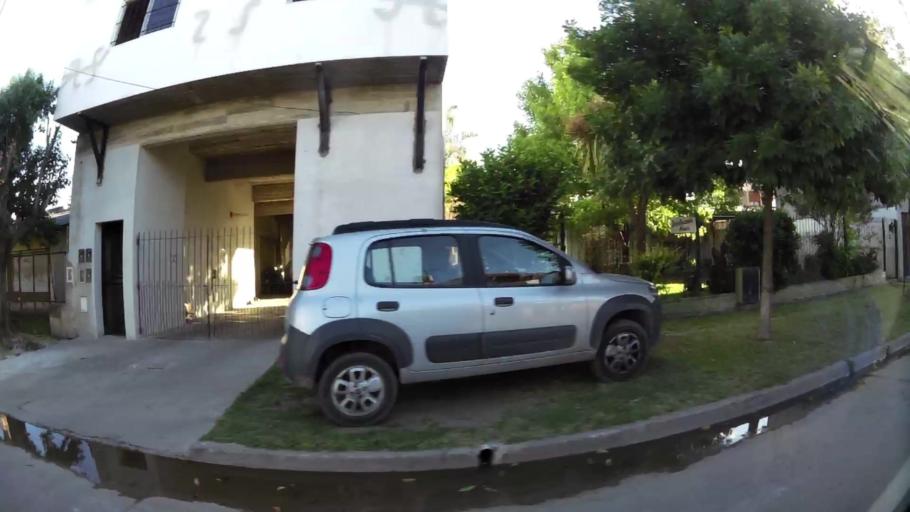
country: AR
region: Buenos Aires
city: Ituzaingo
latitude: -34.6924
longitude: -58.6432
